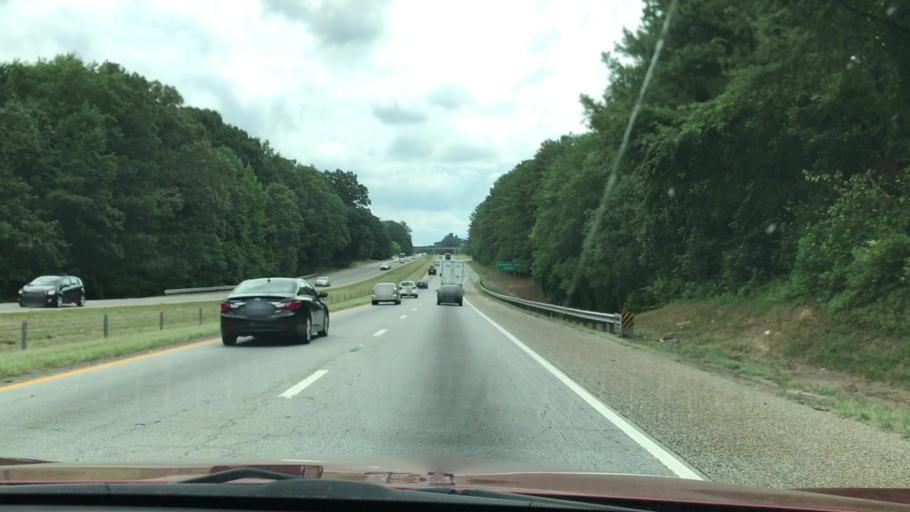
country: US
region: South Carolina
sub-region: Lexington County
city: Chapin
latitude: 34.1810
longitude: -81.3291
